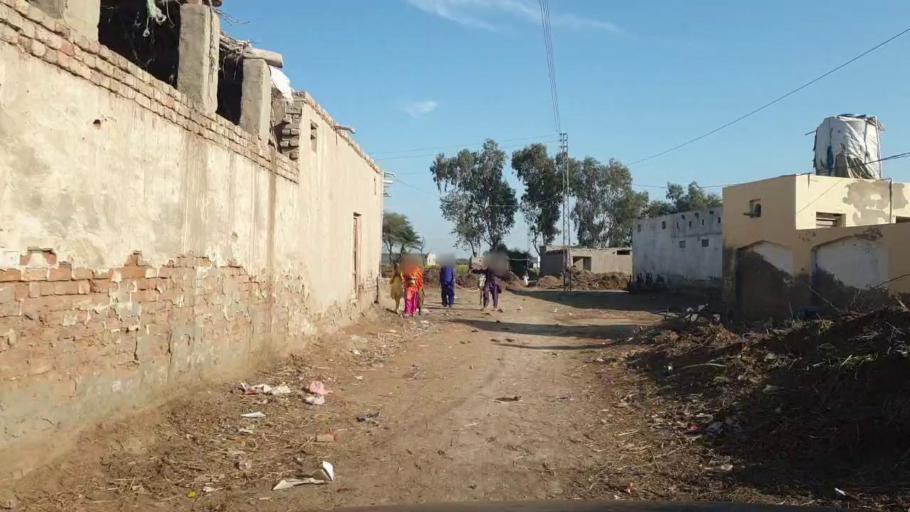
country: PK
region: Sindh
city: Shahpur Chakar
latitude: 26.1823
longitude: 68.6650
